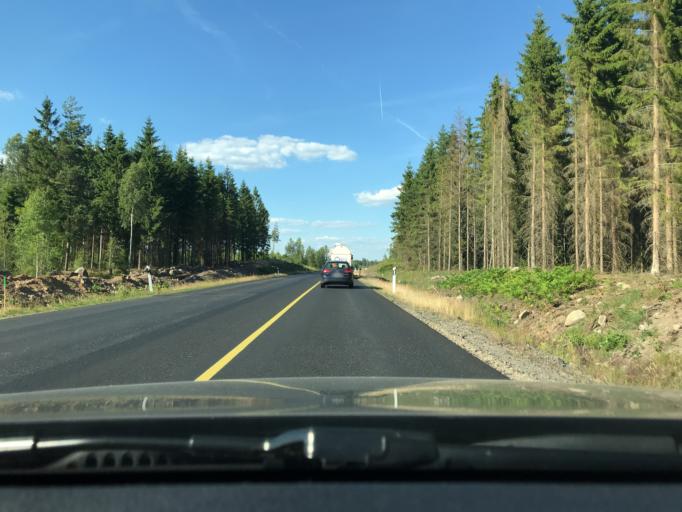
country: SE
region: Kronoberg
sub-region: Almhults Kommun
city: AElmhult
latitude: 56.6149
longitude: 14.2341
